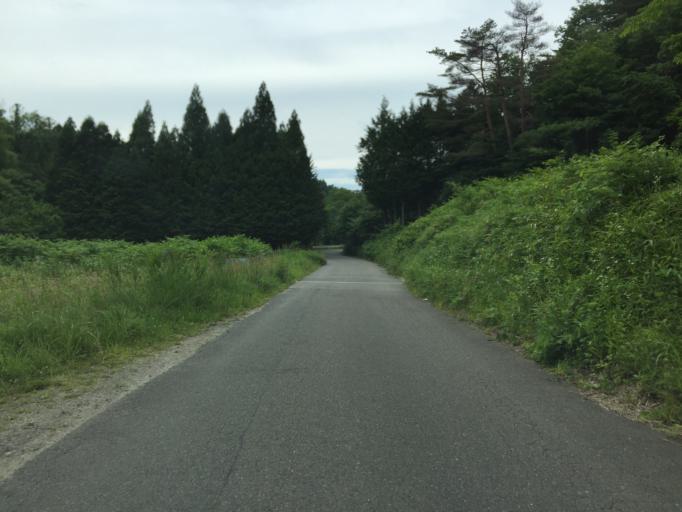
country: JP
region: Fukushima
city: Funehikimachi-funehiki
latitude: 37.4377
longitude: 140.7827
